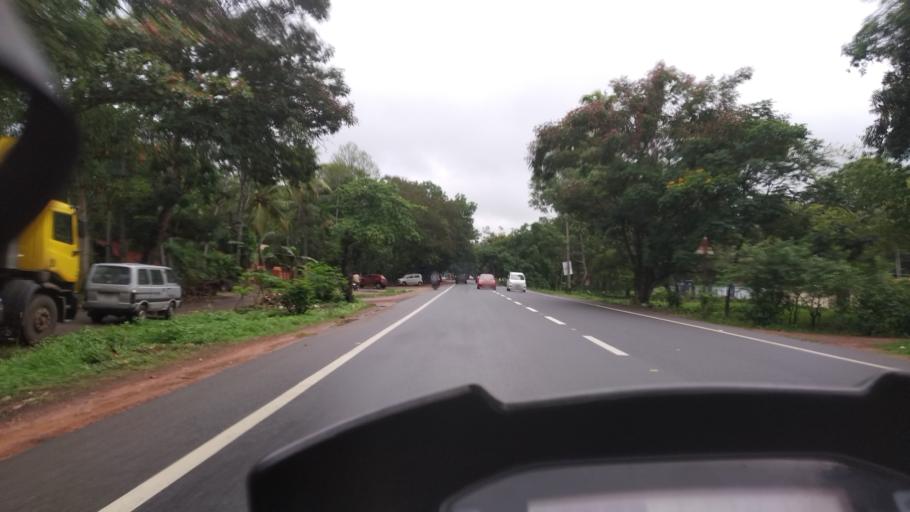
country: IN
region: Kerala
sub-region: Alappuzha
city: Mavelikara
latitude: 9.3039
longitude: 76.4325
